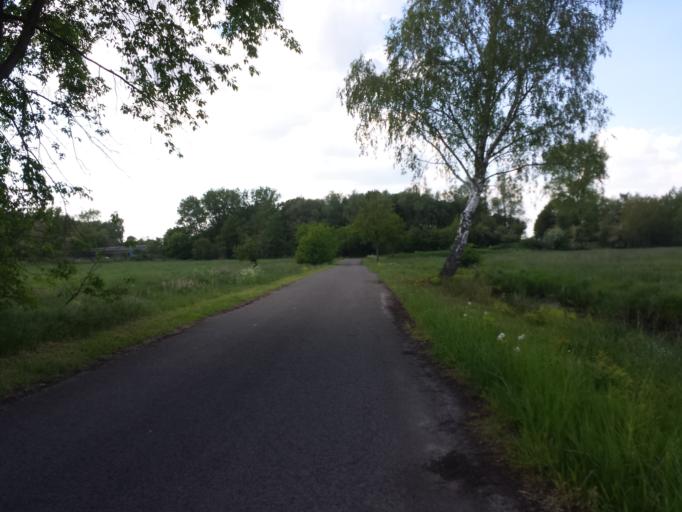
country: DE
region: Bremen
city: Bremen
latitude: 53.1155
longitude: 8.8539
